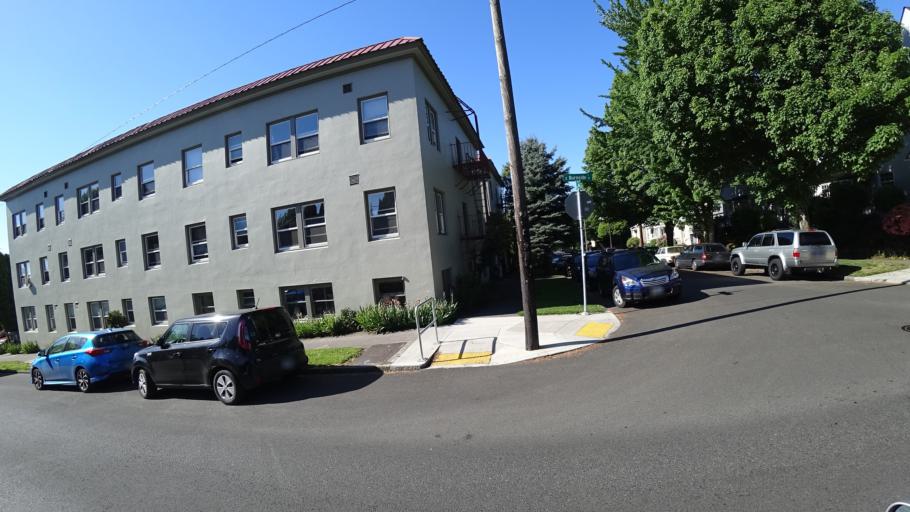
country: US
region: Oregon
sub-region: Multnomah County
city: Portland
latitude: 45.5229
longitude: -122.6332
